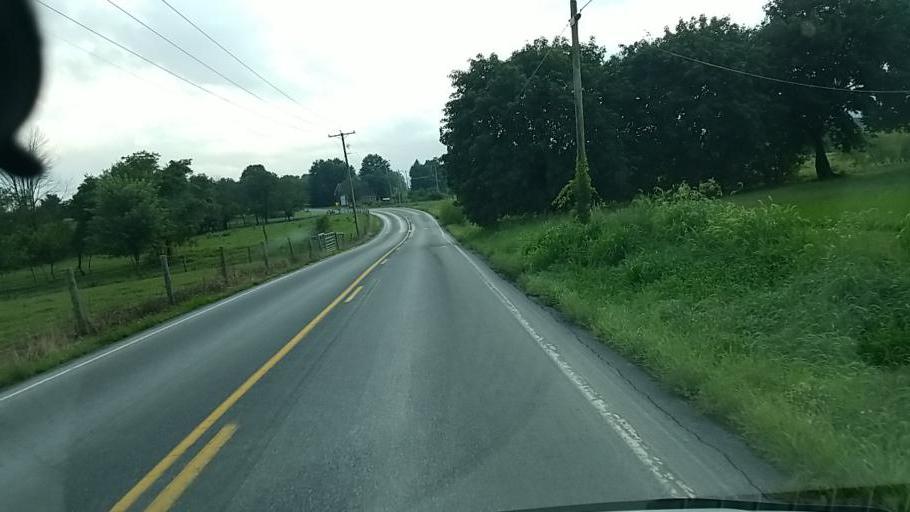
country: US
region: Pennsylvania
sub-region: Cumberland County
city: Shippensburg
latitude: 40.1619
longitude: -77.5771
